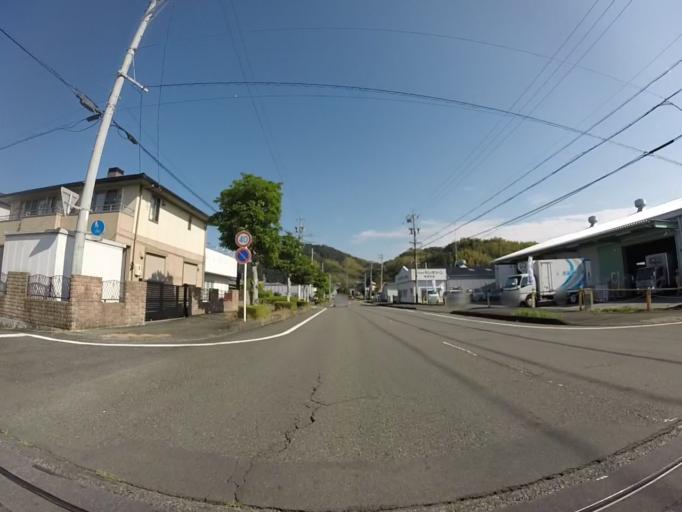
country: JP
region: Shizuoka
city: Fujieda
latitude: 34.8879
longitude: 138.2615
